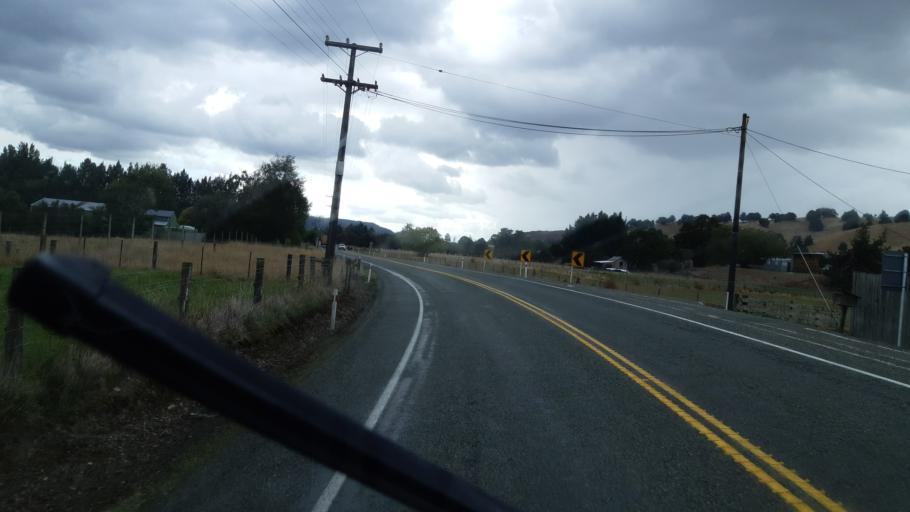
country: NZ
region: Tasman
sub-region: Tasman District
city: Wakefield
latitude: -41.4239
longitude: 173.0013
